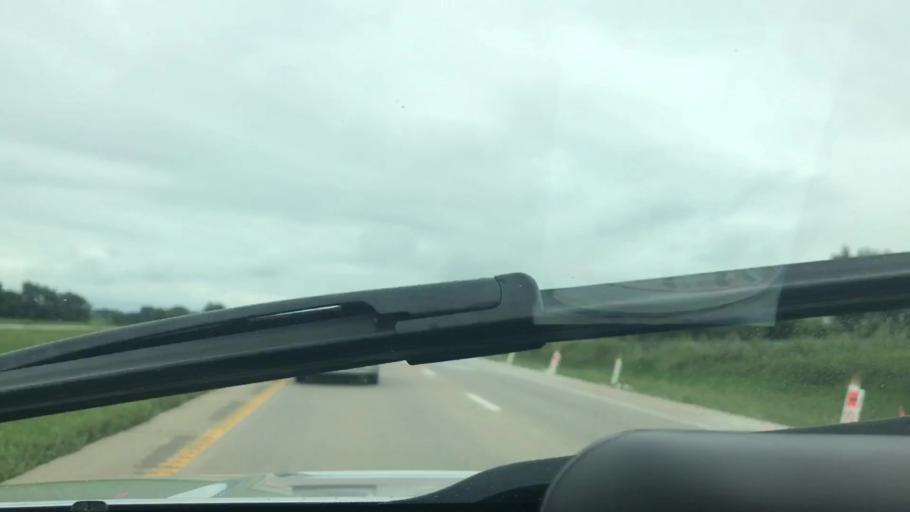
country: US
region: Missouri
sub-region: Jasper County
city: Sarcoxie
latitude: 37.0755
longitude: -93.9948
